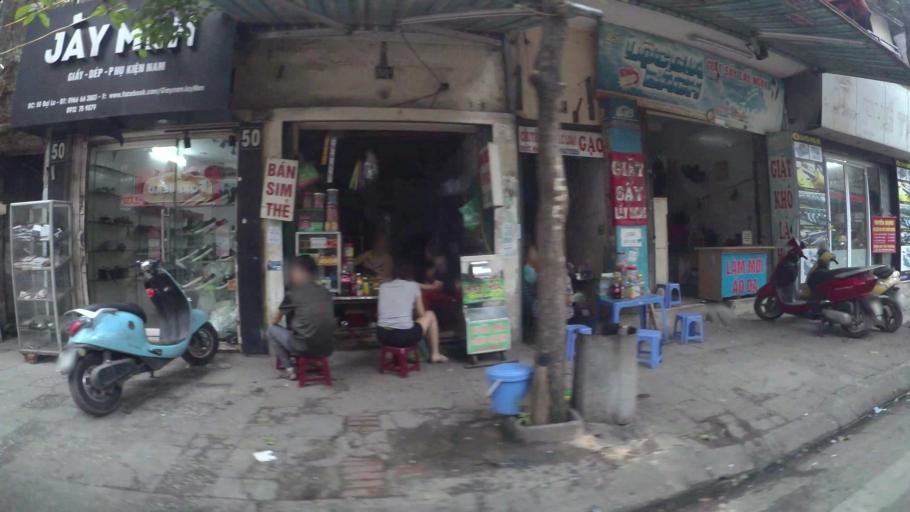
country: VN
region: Ha Noi
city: Hai BaTrung
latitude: 20.9961
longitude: 105.8484
